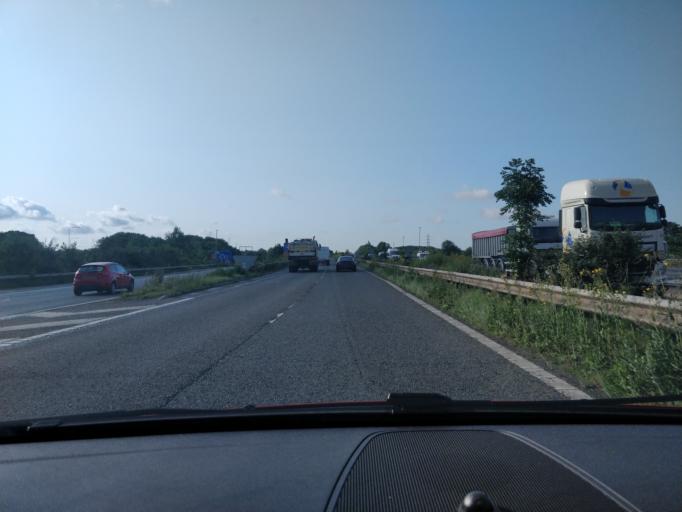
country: GB
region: England
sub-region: Knowsley
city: Whiston
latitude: 53.4022
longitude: -2.8114
